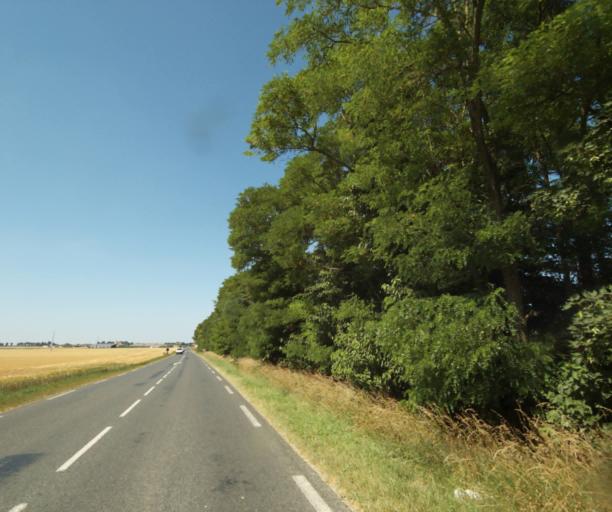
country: FR
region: Ile-de-France
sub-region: Departement de Seine-et-Marne
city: La Chapelle-la-Reine
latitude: 48.3001
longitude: 2.5738
